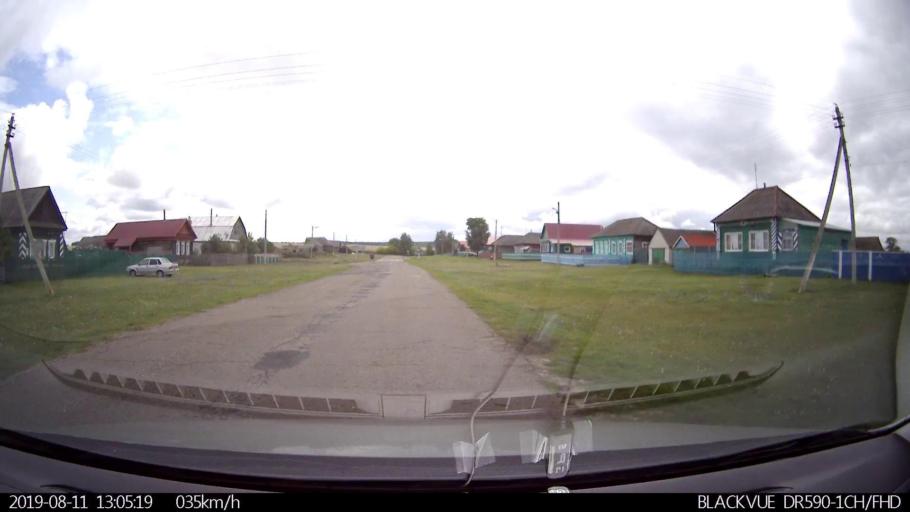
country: RU
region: Ulyanovsk
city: Ignatovka
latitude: 53.8713
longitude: 47.6493
